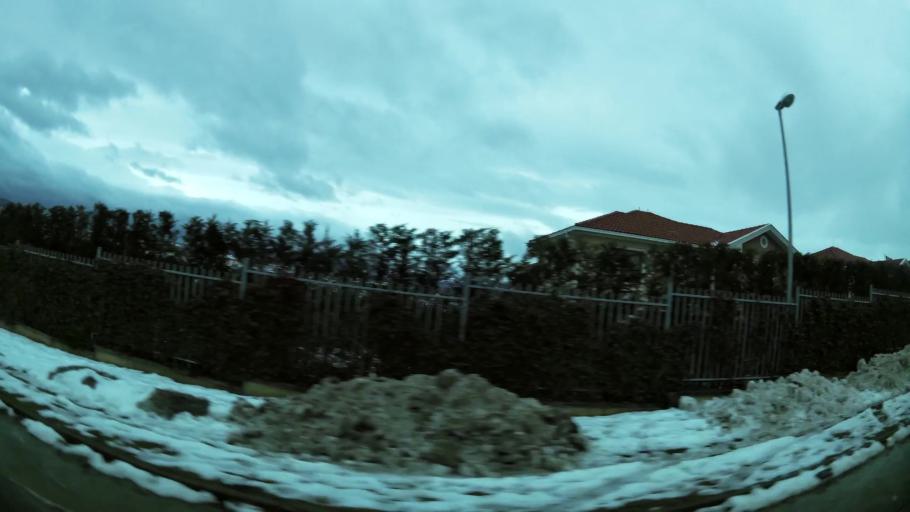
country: XK
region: Pristina
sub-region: Komuna e Prishtines
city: Pristina
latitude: 42.6312
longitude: 21.1680
